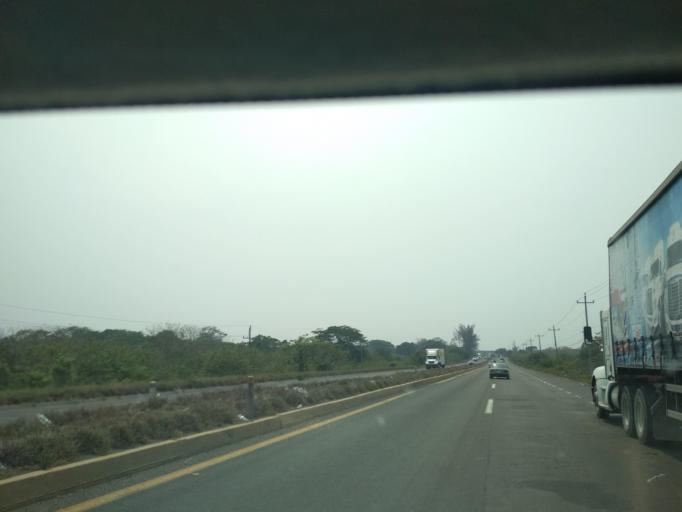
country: MX
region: Veracruz
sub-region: Veracruz
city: Delfino Victoria (Santa Fe)
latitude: 19.1856
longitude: -96.2657
